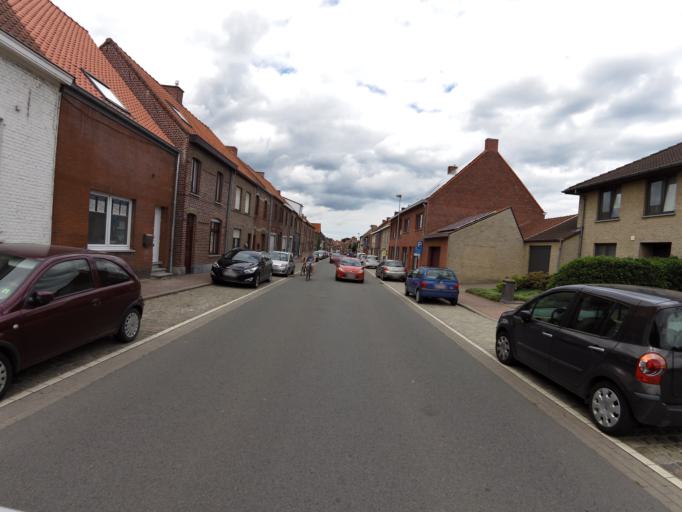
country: BE
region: Flanders
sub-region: Provincie West-Vlaanderen
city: Kortemark
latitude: 51.0237
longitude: 3.0440
